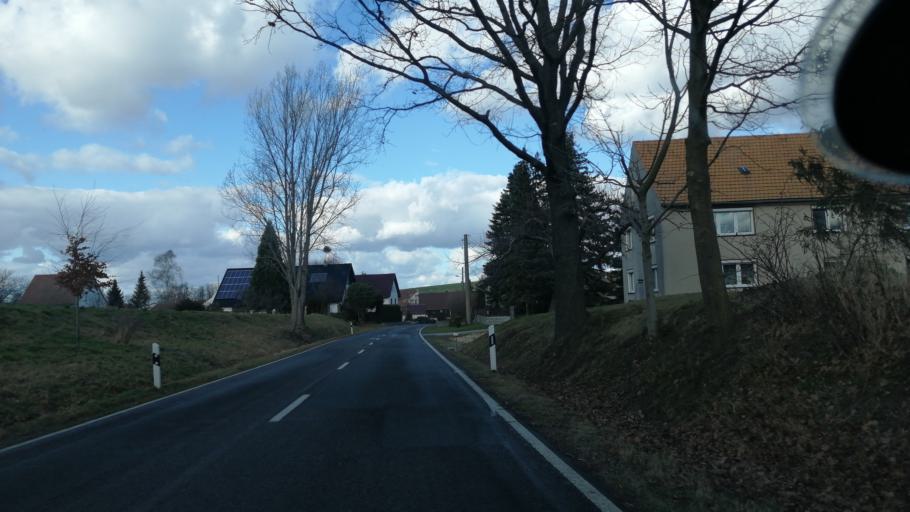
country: DE
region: Saxony
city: Kubschutz
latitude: 51.1415
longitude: 14.5350
